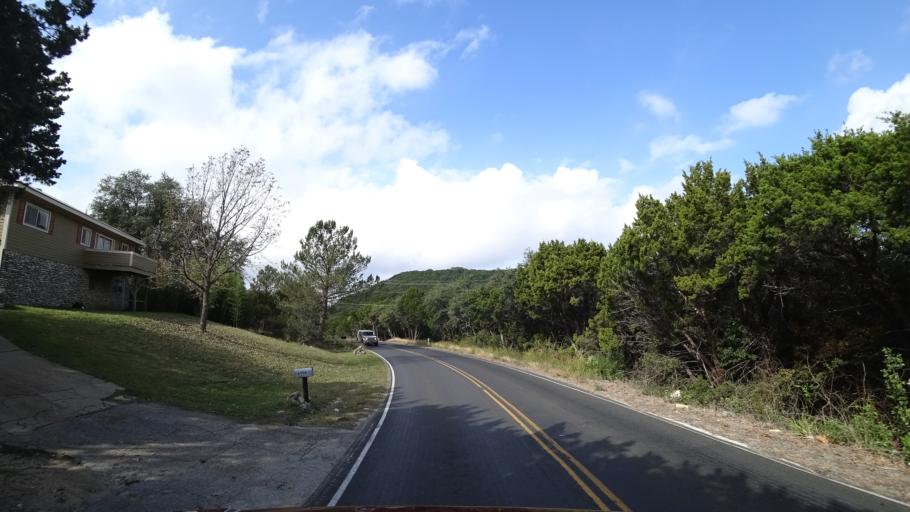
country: US
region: Texas
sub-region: Travis County
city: Hudson Bend
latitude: 30.4133
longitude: -97.8777
